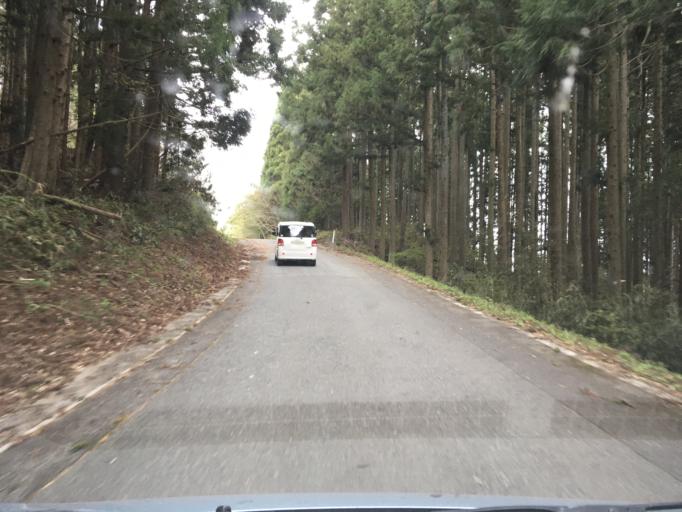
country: JP
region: Iwate
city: Ichinoseki
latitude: 38.9659
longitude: 141.1925
